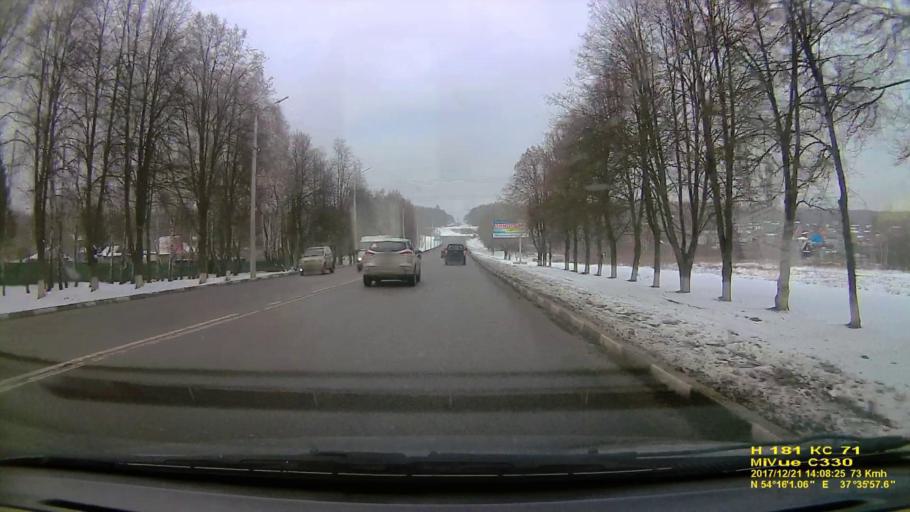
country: RU
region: Tula
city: Gorelki
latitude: 54.2672
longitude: 37.5991
